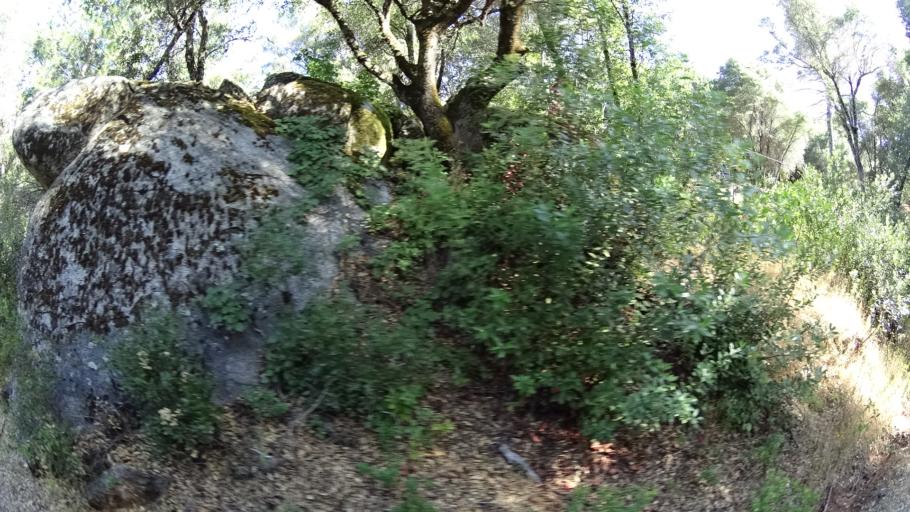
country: US
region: California
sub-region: Amador County
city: Pioneer
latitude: 38.3931
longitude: -120.5702
